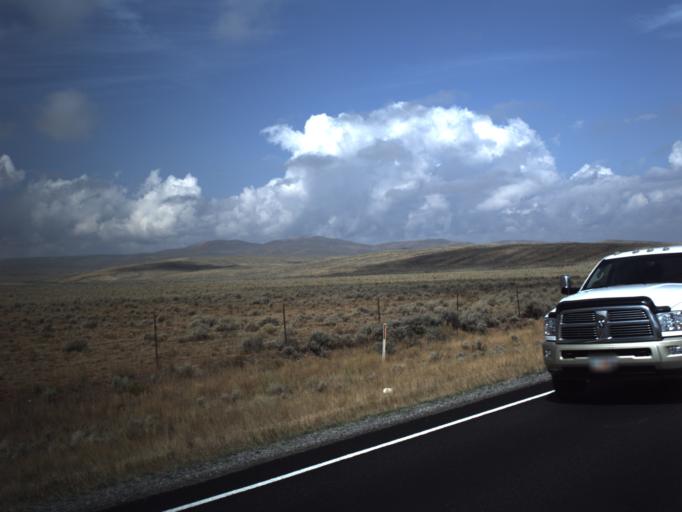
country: US
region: Utah
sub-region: Rich County
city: Randolph
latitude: 41.5659
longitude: -111.1592
